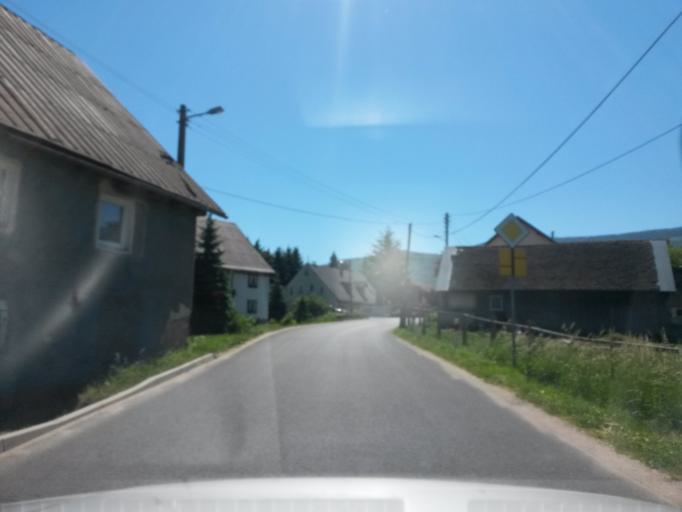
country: PL
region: Lower Silesian Voivodeship
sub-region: Powiat jeleniogorski
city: Karpacz
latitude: 50.7988
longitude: 15.7761
